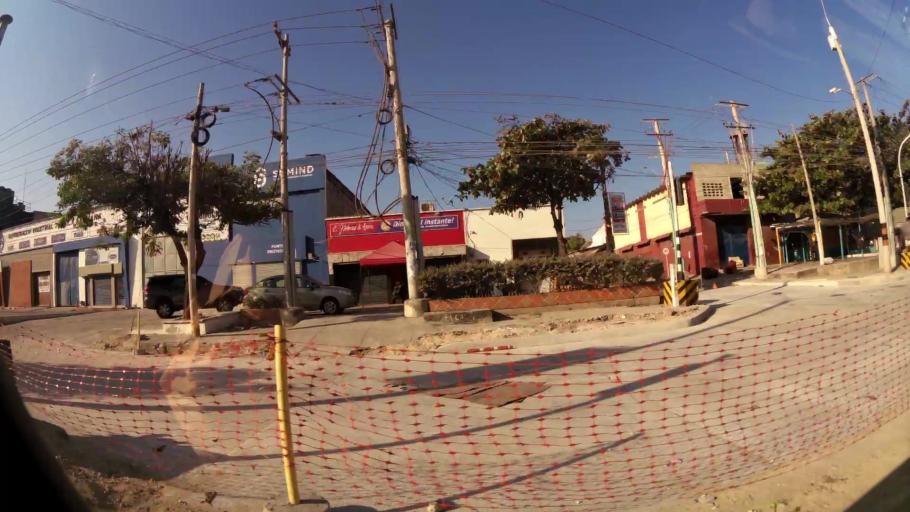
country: CO
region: Atlantico
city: Barranquilla
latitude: 11.0262
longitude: -74.8038
